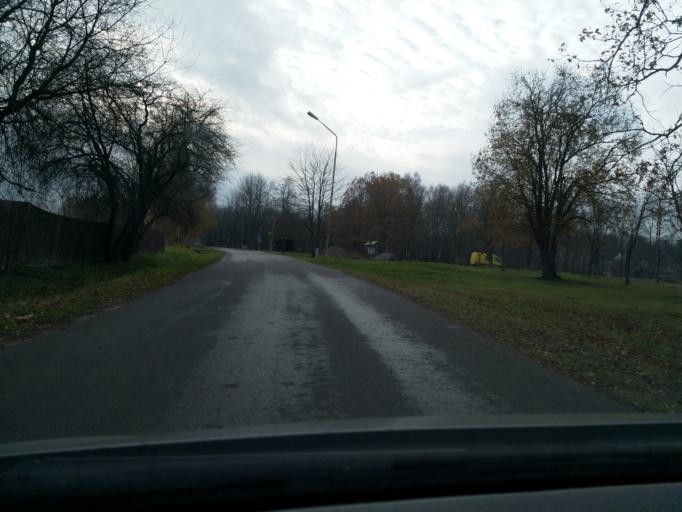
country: LV
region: Kuldigas Rajons
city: Kuldiga
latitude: 56.9735
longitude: 21.9778
